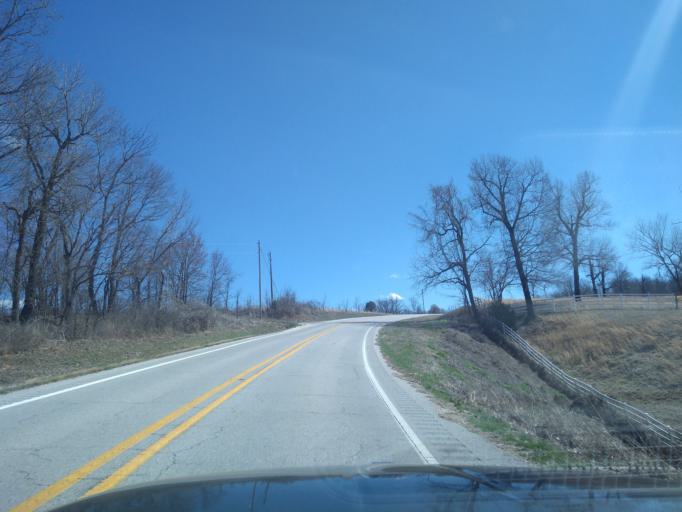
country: US
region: Arkansas
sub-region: Washington County
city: Farmington
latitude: 36.0966
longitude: -94.3339
